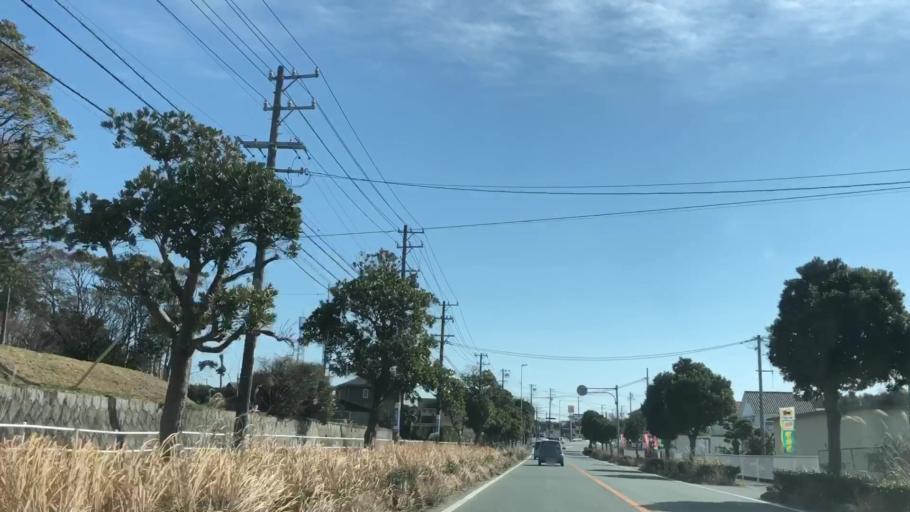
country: JP
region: Aichi
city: Toyohashi
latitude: 34.7028
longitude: 137.4135
